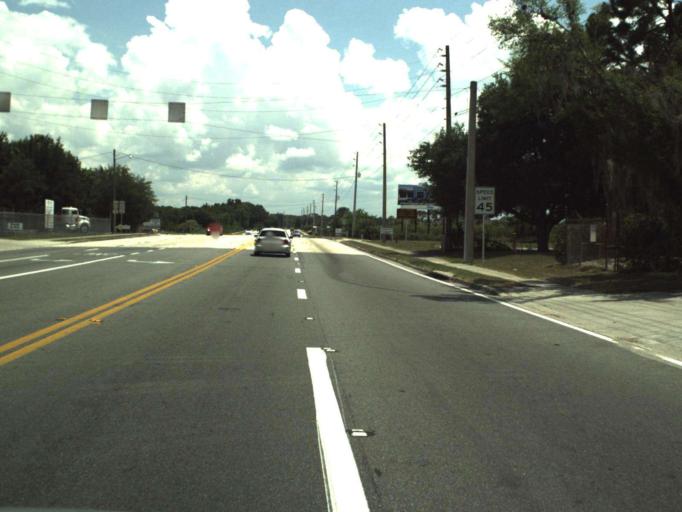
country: US
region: Florida
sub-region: Lake County
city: Leesburg
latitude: 28.8116
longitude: -81.9165
